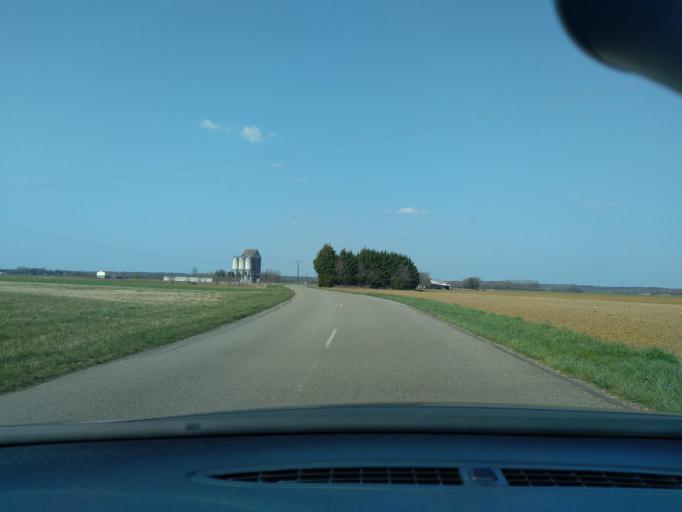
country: FR
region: Franche-Comte
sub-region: Departement du Jura
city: Mont-sous-Vaudrey
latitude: 46.9873
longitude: 5.6059
